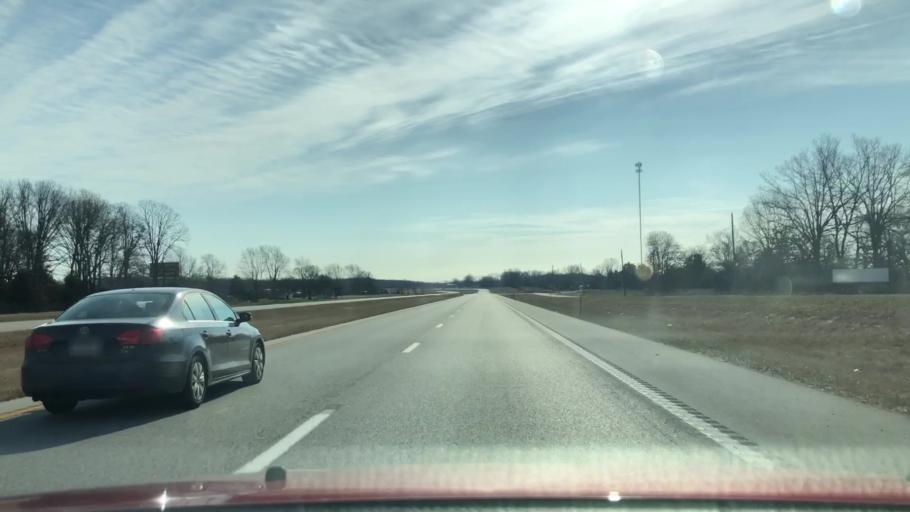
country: US
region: Missouri
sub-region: Webster County
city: Seymour
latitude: 37.1414
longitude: -92.7463
